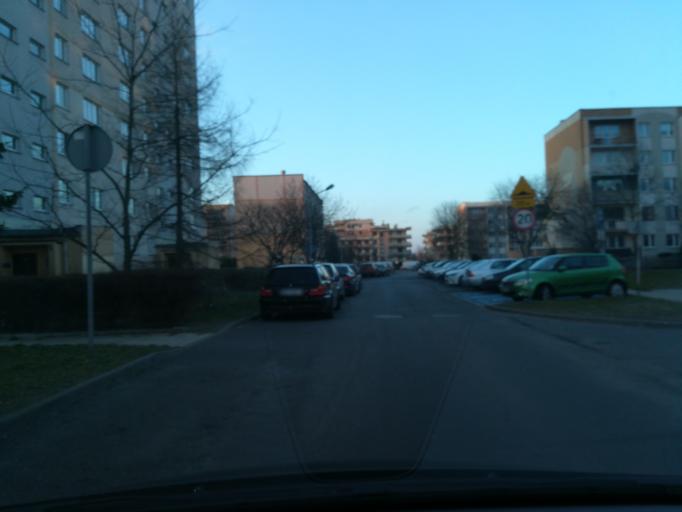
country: PL
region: Lodz Voivodeship
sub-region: Piotrkow Trybunalski
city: Piotrkow Trybunalski
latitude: 51.4113
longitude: 19.6595
